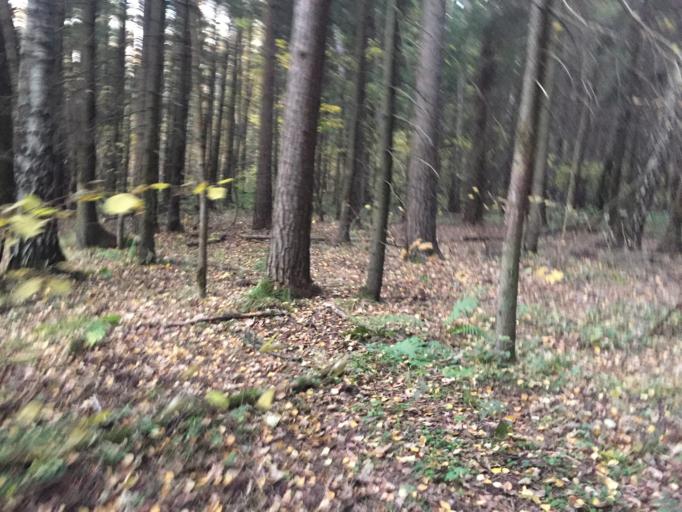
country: RU
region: Moscow
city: Gol'yanovo
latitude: 55.8576
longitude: 37.7830
